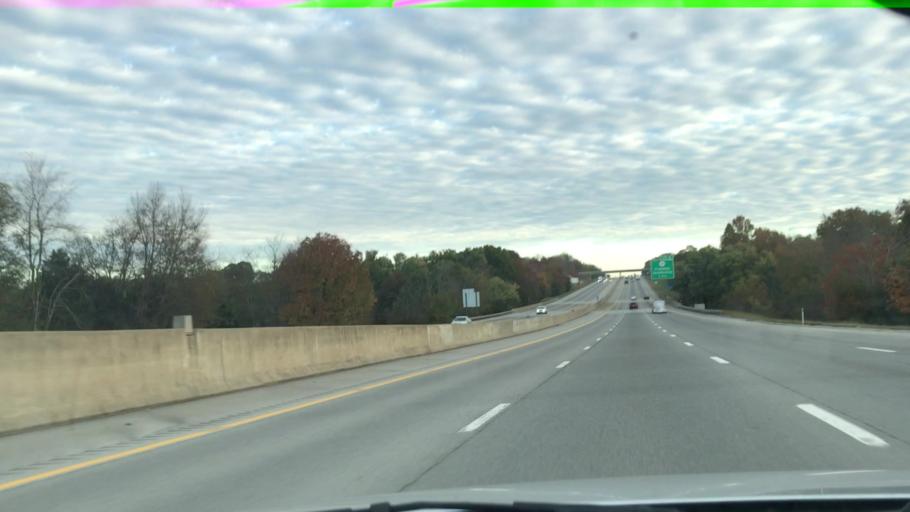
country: US
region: Kentucky
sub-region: Simpson County
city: Franklin
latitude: 36.6922
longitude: -86.5346
